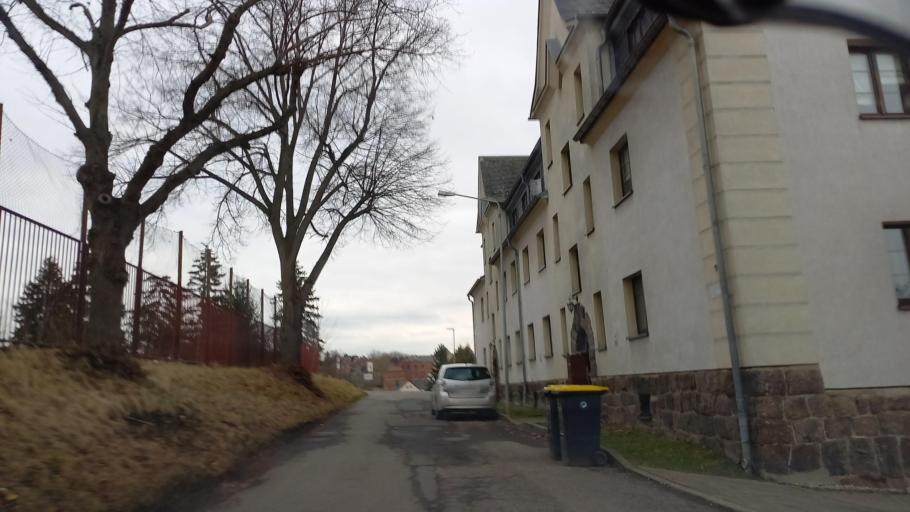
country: DE
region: Saxony
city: Wilkau-Hasslau
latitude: 50.6790
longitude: 12.5167
